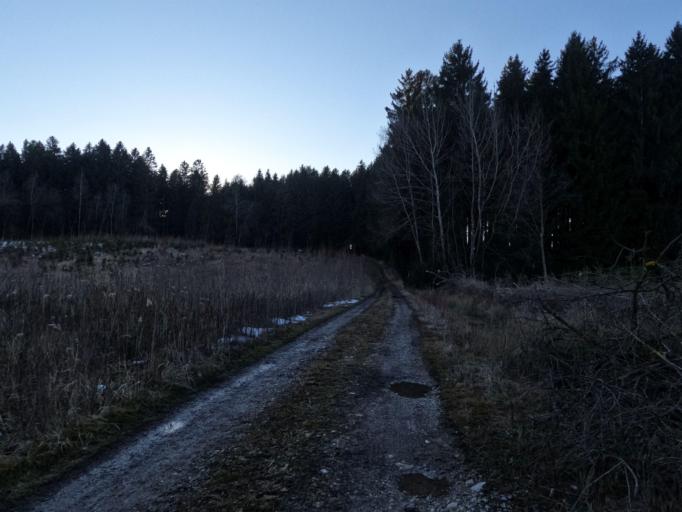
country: DE
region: Bavaria
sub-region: Upper Bavaria
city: Chieming
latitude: 47.8725
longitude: 12.5736
